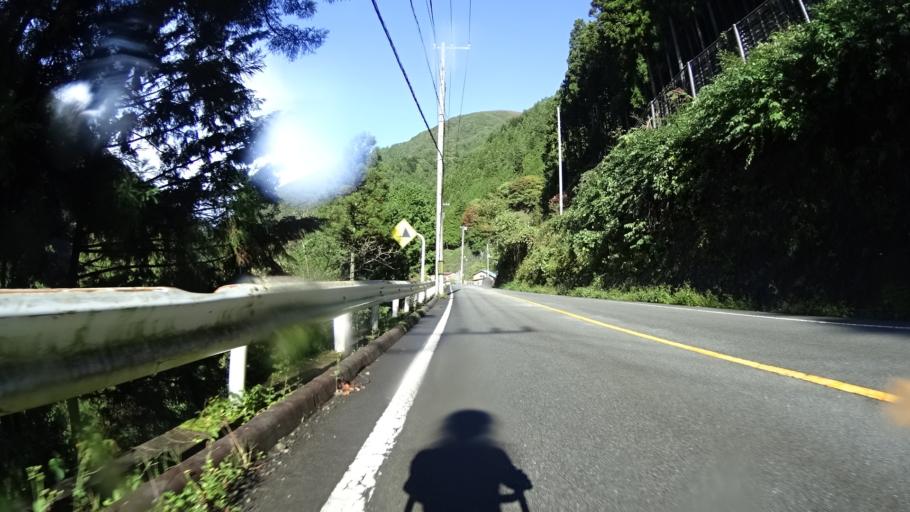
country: JP
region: Yamanashi
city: Otsuki
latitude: 35.7873
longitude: 138.9459
